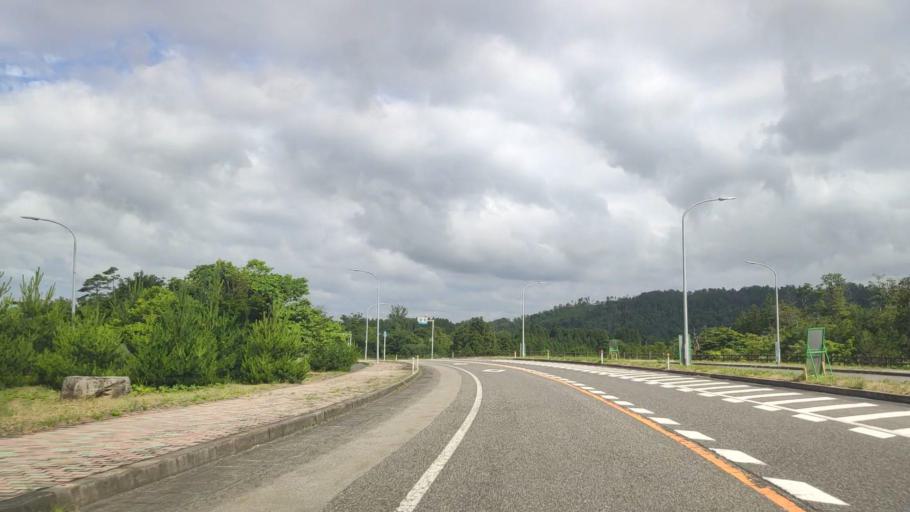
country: JP
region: Tottori
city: Yonago
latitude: 35.4173
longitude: 133.4584
